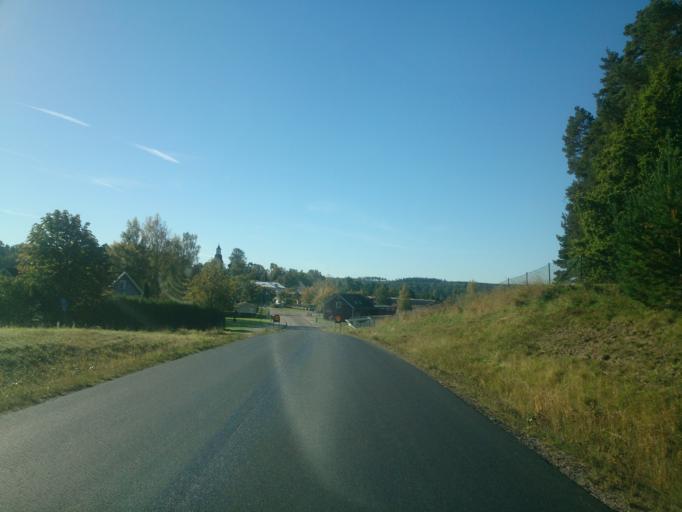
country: SE
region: OEstergoetland
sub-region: Linkopings Kommun
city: Sturefors
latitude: 58.3029
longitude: 15.8656
